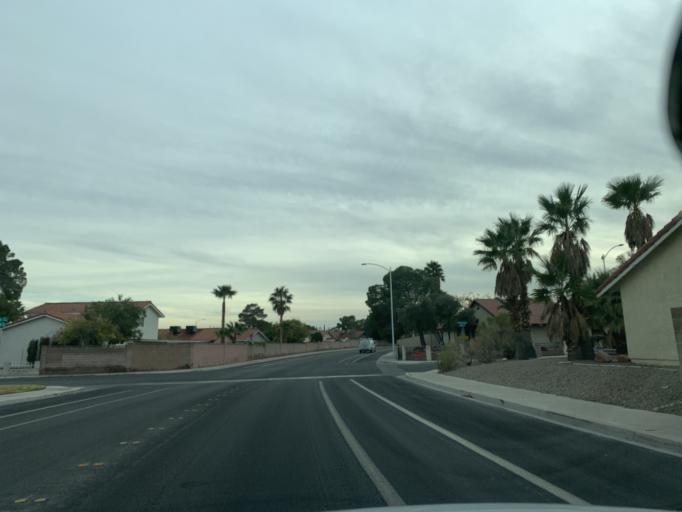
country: US
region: Nevada
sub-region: Clark County
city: Summerlin South
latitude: 36.1572
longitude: -115.2870
